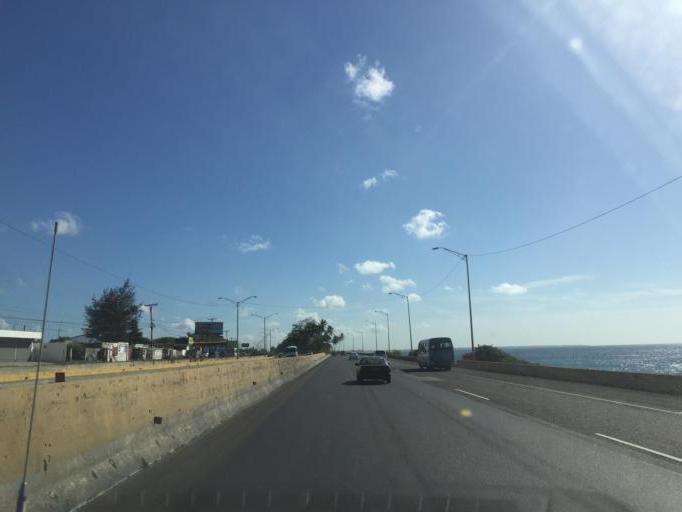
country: DO
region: Santo Domingo
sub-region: Santo Domingo
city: Santo Domingo Este
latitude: 18.4644
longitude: -69.7683
